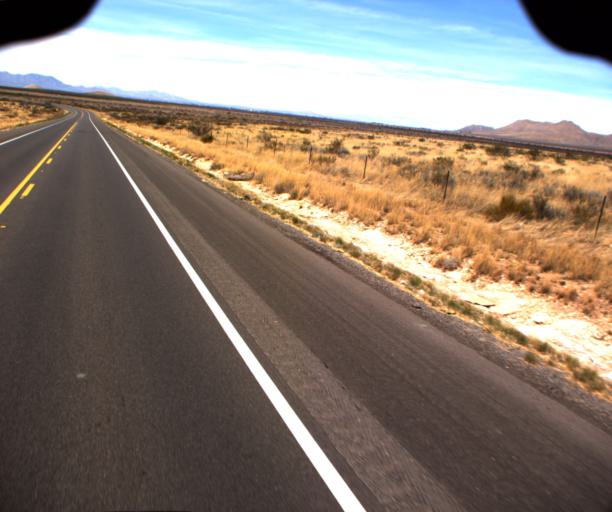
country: US
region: Arizona
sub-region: Cochise County
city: Willcox
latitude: 31.9031
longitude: -109.7144
